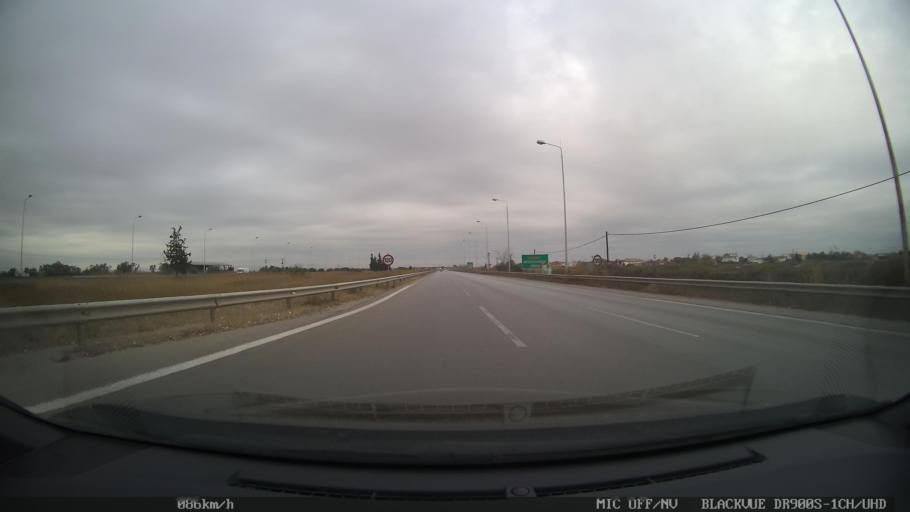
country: GR
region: Central Macedonia
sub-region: Nomos Thessalonikis
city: Kymina
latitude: 40.6018
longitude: 22.6926
